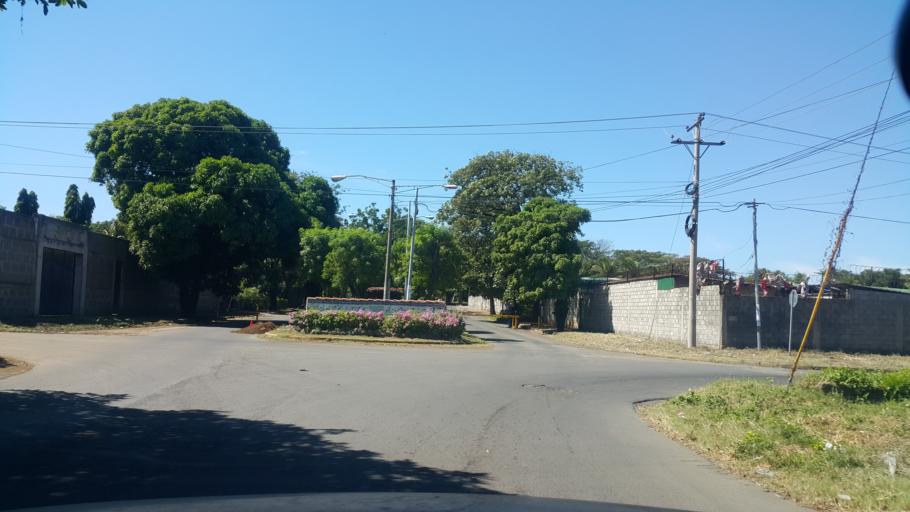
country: NI
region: Managua
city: Ciudad Sandino
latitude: 12.1439
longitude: -86.3368
